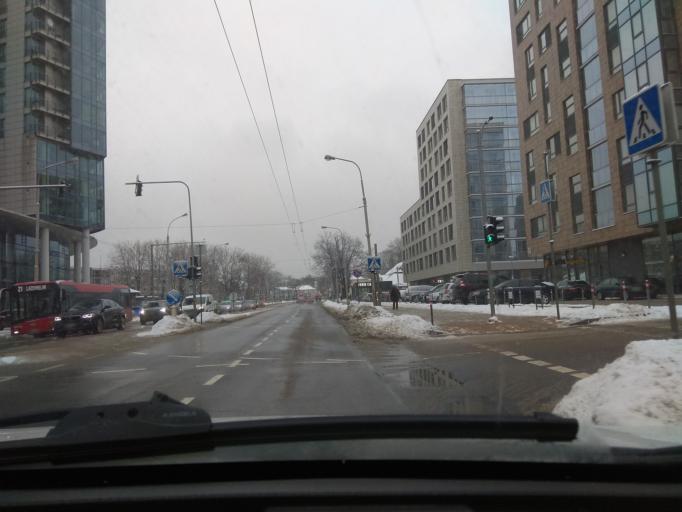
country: LT
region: Vilnius County
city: Naujamiestis
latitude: 54.6786
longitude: 25.2573
